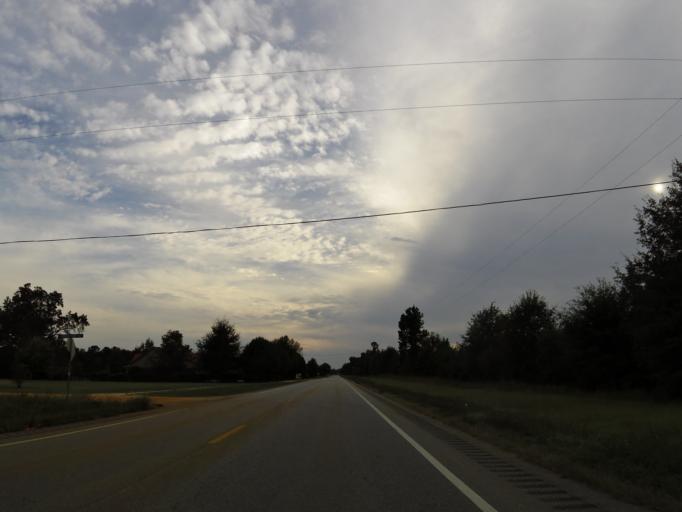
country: US
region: Alabama
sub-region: Monroe County
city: Frisco City
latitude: 31.3553
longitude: -87.4410
